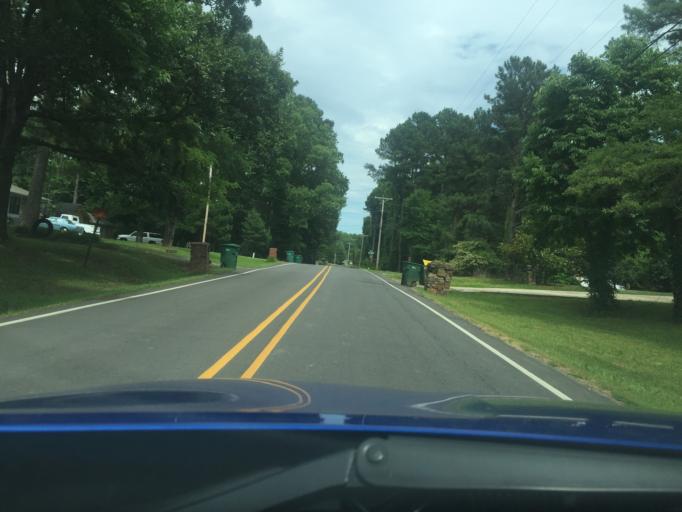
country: US
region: Arkansas
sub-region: Pulaski County
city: Maumelle
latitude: 34.8310
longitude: -92.4468
